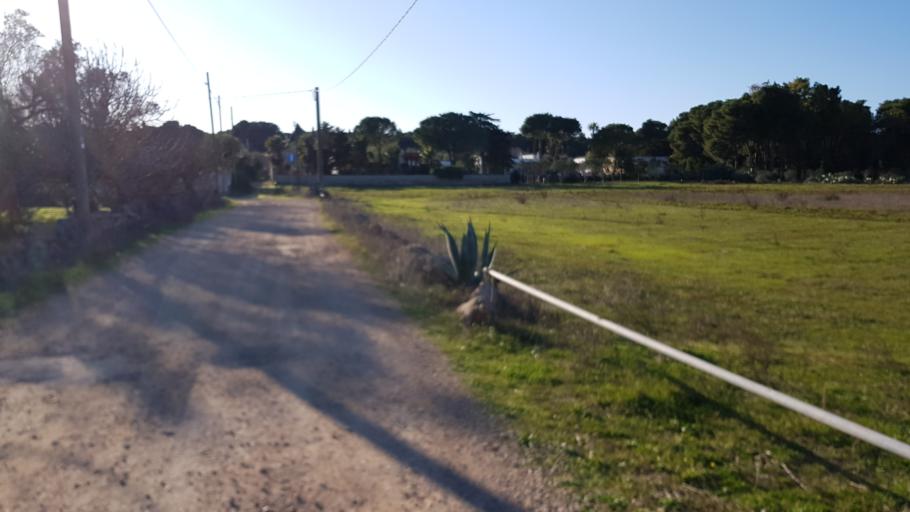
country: IT
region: Apulia
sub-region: Provincia di Lecce
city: Nardo
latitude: 40.1607
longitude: 17.9706
